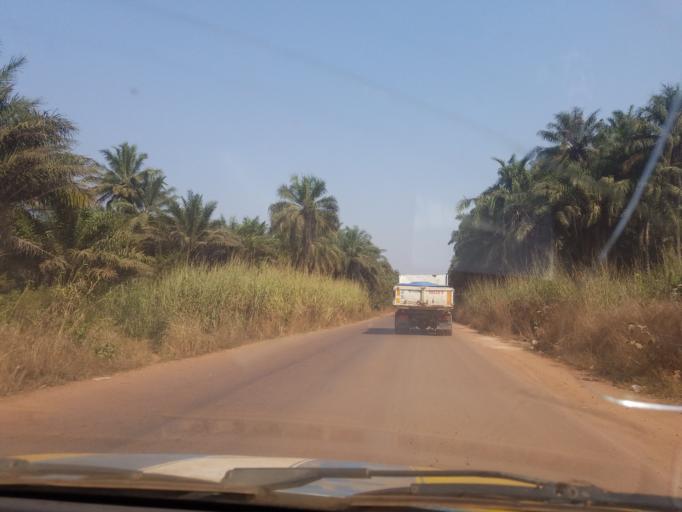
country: GN
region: Boke
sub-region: Boke Prefecture
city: Boke
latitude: 10.8346
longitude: -14.3619
